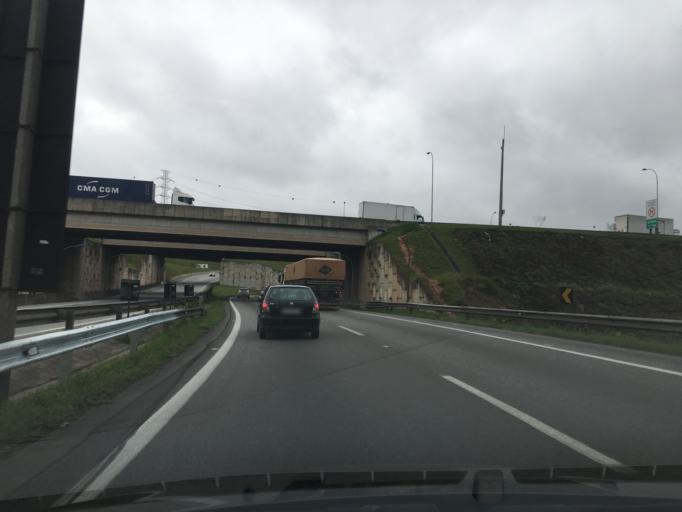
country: BR
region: Sao Paulo
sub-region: Embu
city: Embu
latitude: -23.6311
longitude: -46.8320
